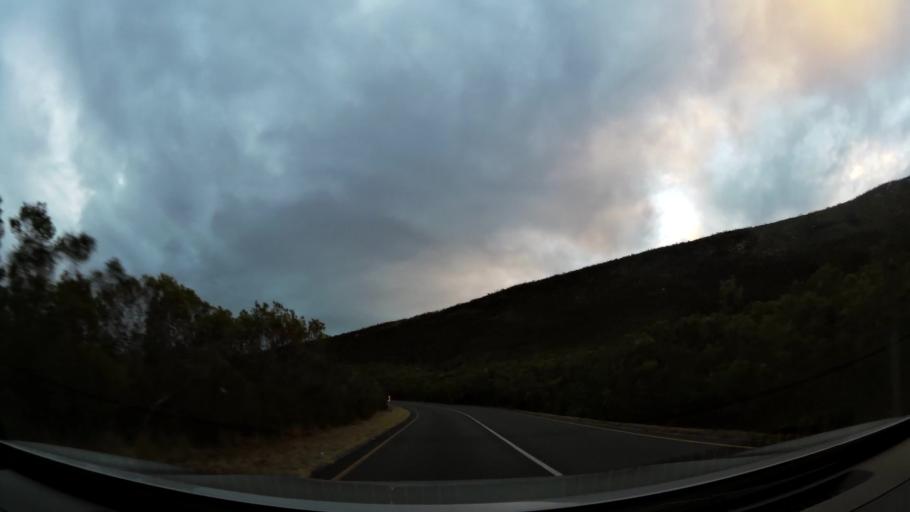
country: ZA
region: Western Cape
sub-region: Overberg District Municipality
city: Swellendam
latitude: -33.9865
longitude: 20.7139
